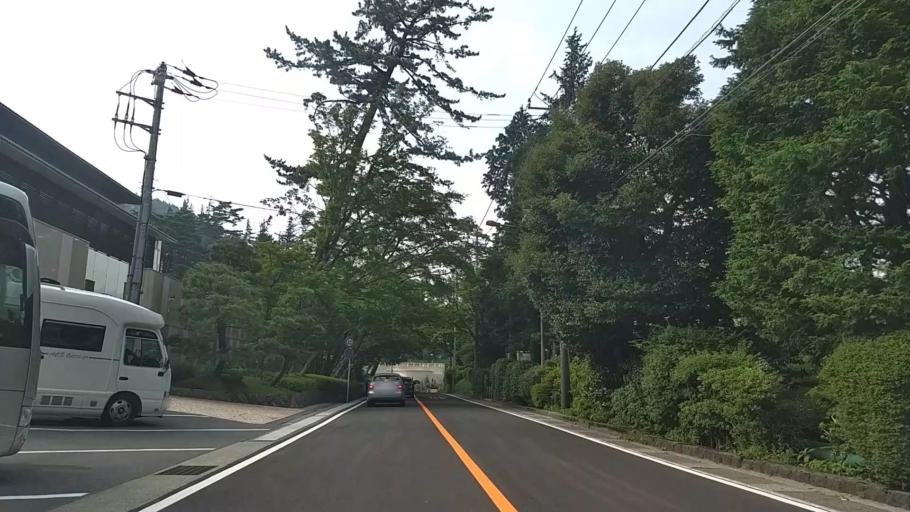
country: JP
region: Kanagawa
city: Hakone
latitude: 35.2376
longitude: 139.0469
